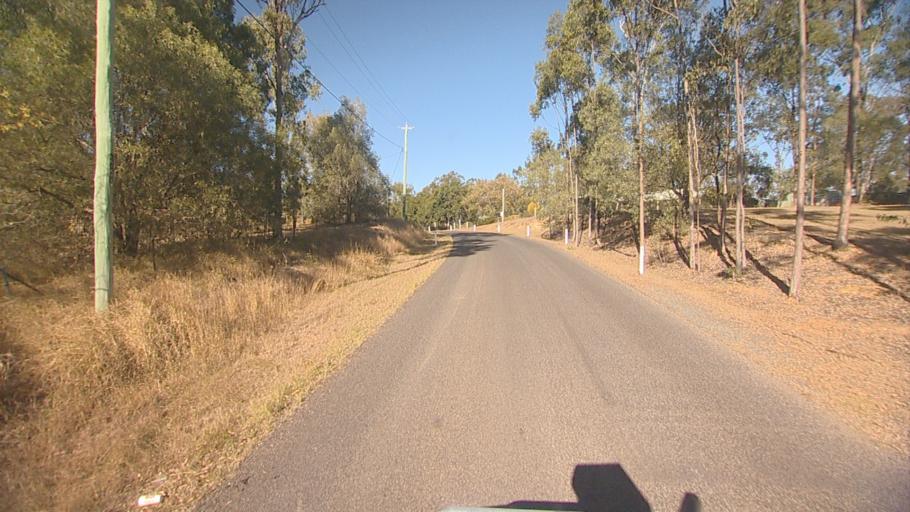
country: AU
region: Queensland
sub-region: Logan
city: North Maclean
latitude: -27.8312
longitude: 152.9896
